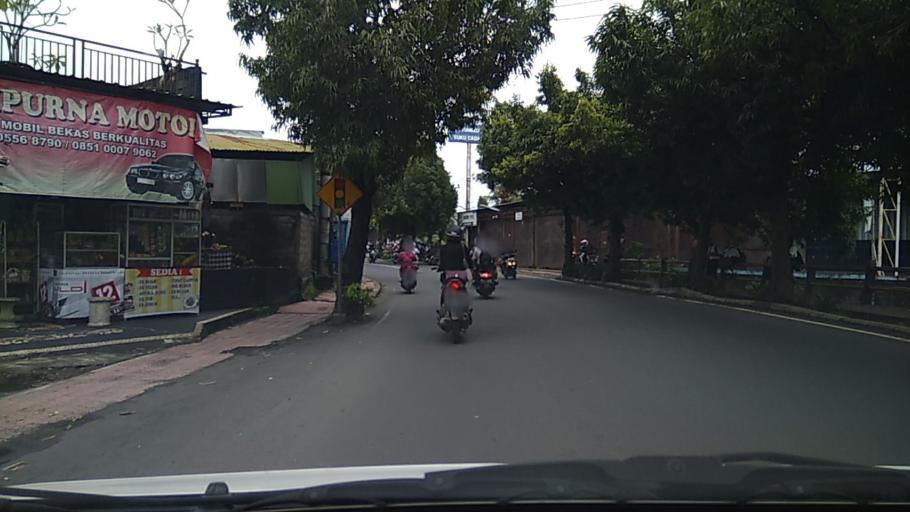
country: ID
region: Bali
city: Banjar Kelodan
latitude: -8.5406
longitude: 115.3467
